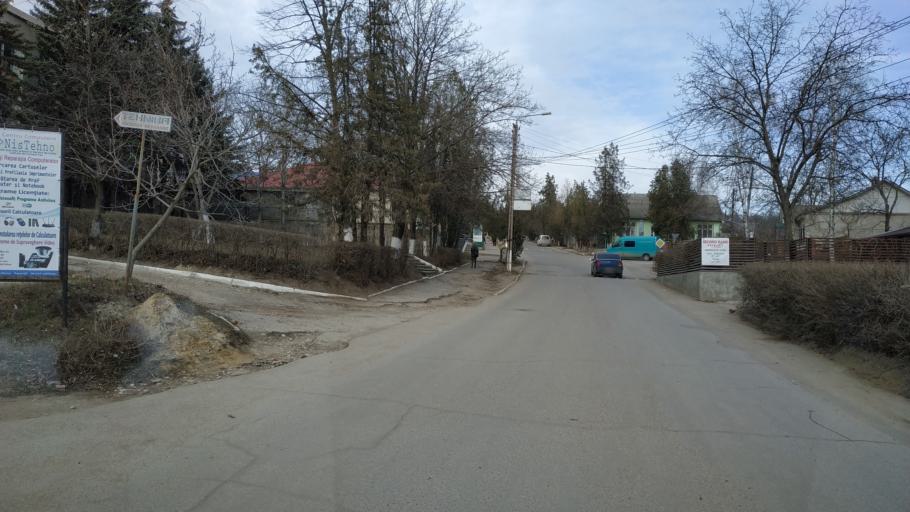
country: MD
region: Nisporeni
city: Nisporeni
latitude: 47.0809
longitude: 28.1878
